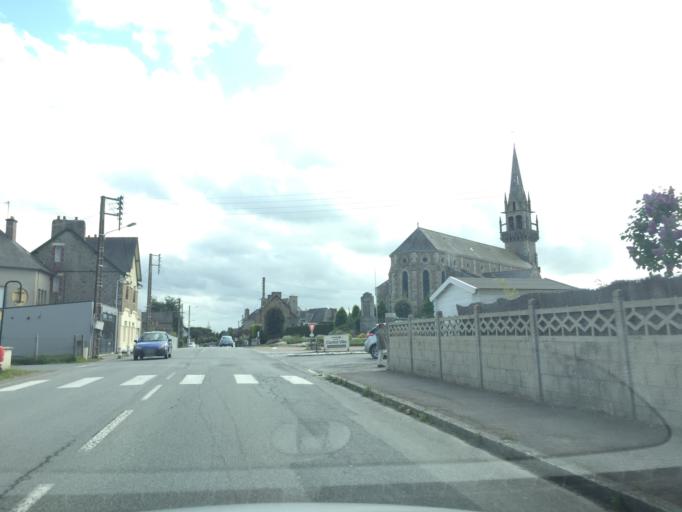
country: FR
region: Brittany
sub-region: Departement des Cotes-d'Armor
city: Lancieux
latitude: 48.6083
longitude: -2.1485
